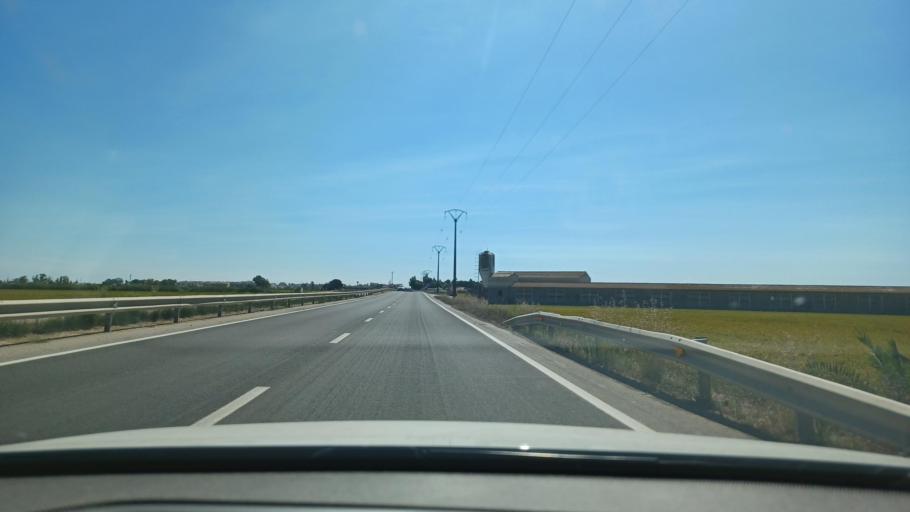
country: ES
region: Catalonia
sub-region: Provincia de Tarragona
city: Deltebre
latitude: 40.7070
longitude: 0.6993
